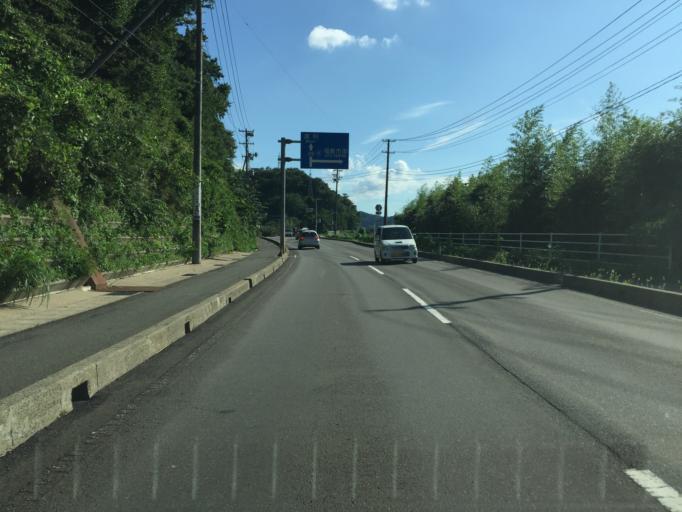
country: JP
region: Fukushima
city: Fukushima-shi
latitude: 37.7596
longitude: 140.4894
